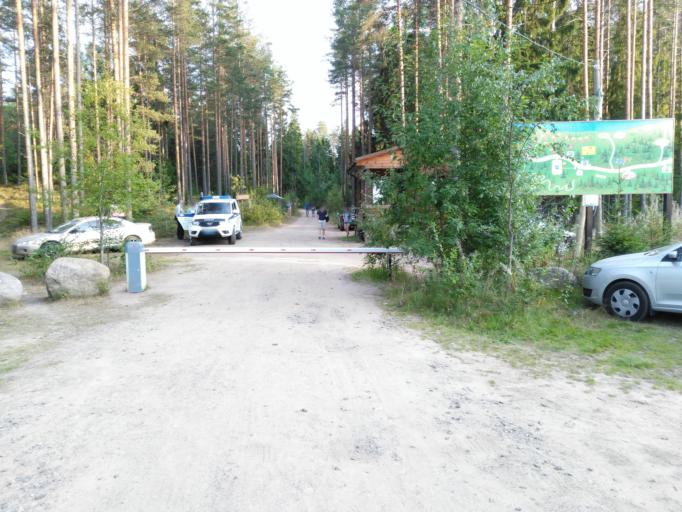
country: RU
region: Leningrad
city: Il'ichevo
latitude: 60.2849
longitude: 29.7435
